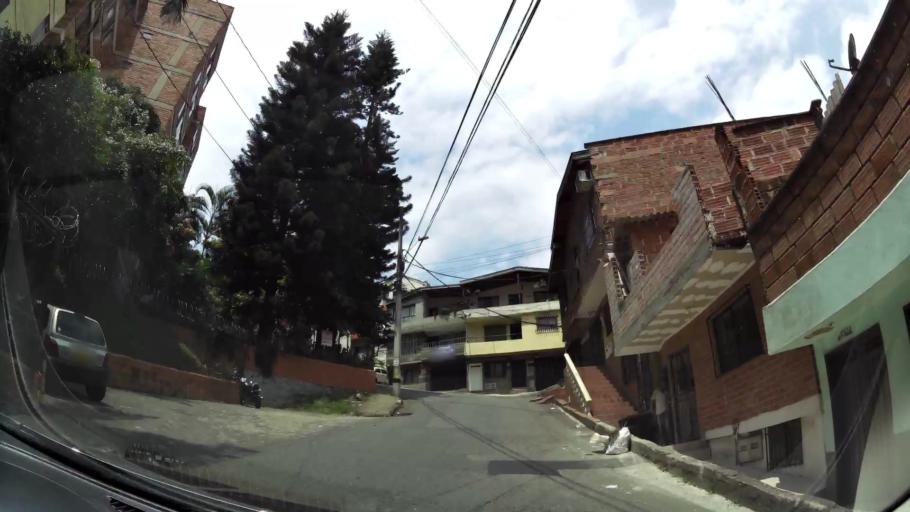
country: CO
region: Antioquia
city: Medellin
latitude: 6.2603
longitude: -75.5555
